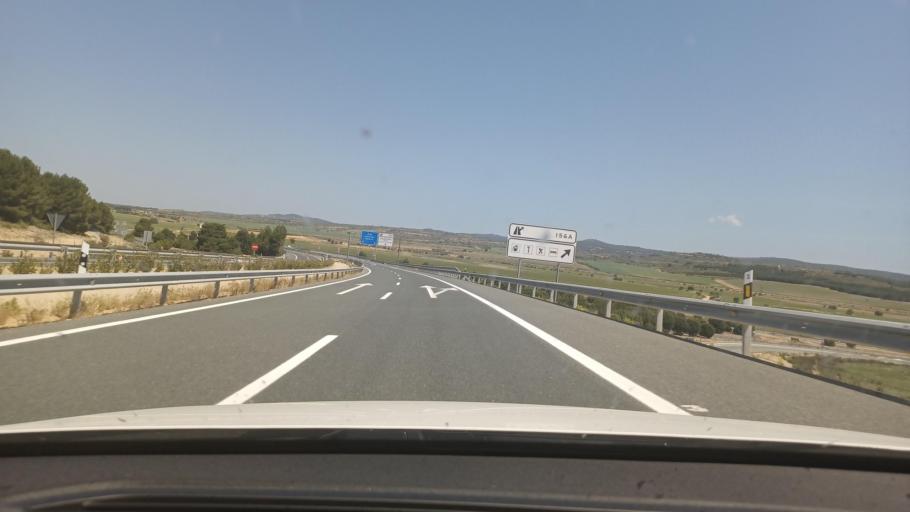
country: ES
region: Castille-La Mancha
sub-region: Provincia de Albacete
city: Almansa
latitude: 38.8449
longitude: -1.0142
